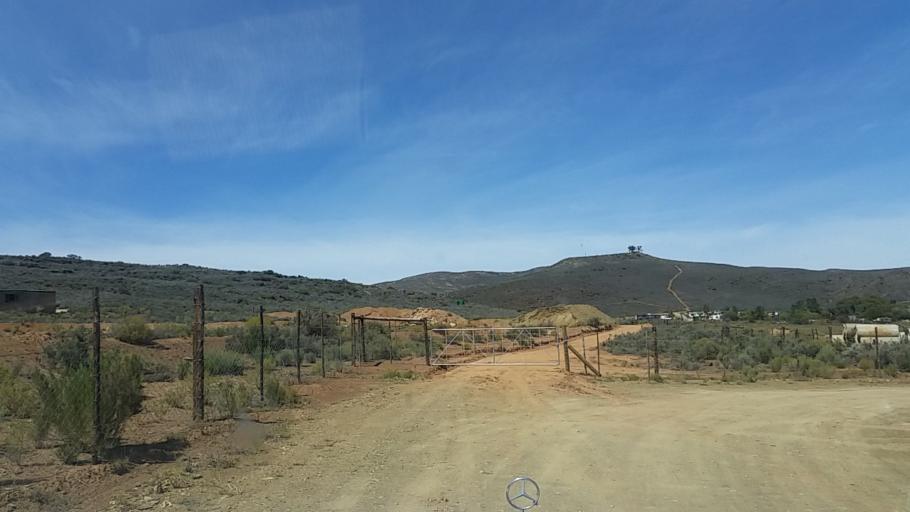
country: ZA
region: Western Cape
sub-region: Eden District Municipality
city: Knysna
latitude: -33.6491
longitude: 23.1378
